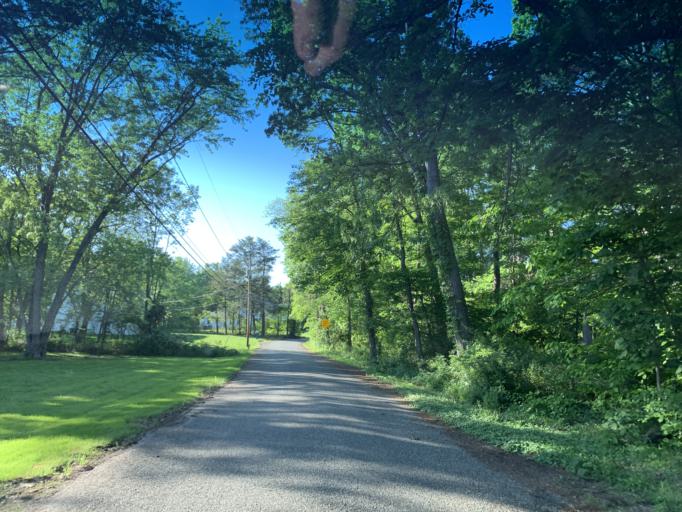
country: US
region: Maryland
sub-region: Harford County
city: Riverside
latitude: 39.4651
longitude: -76.2635
